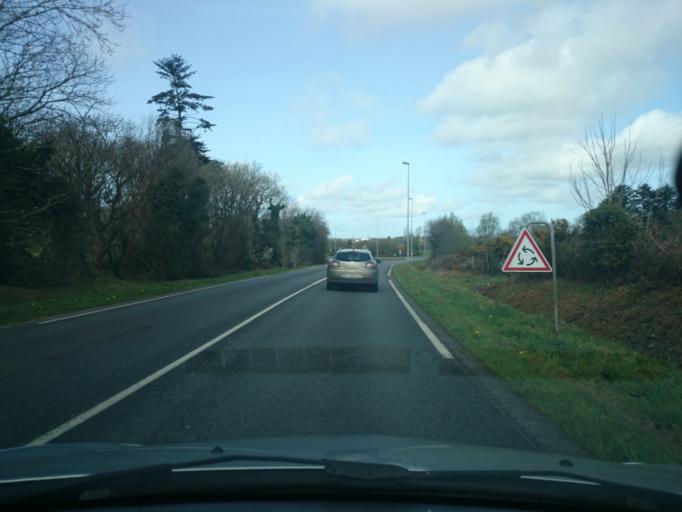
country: FR
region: Brittany
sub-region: Departement du Finistere
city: Gouesnou
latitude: 48.4426
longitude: -4.4546
